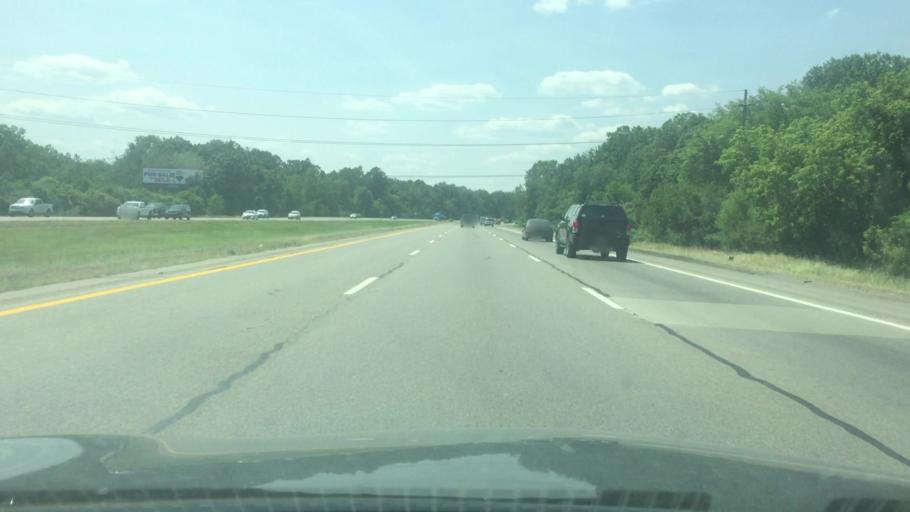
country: US
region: Michigan
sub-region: Wayne County
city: Romulus
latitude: 42.2298
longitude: -83.4248
